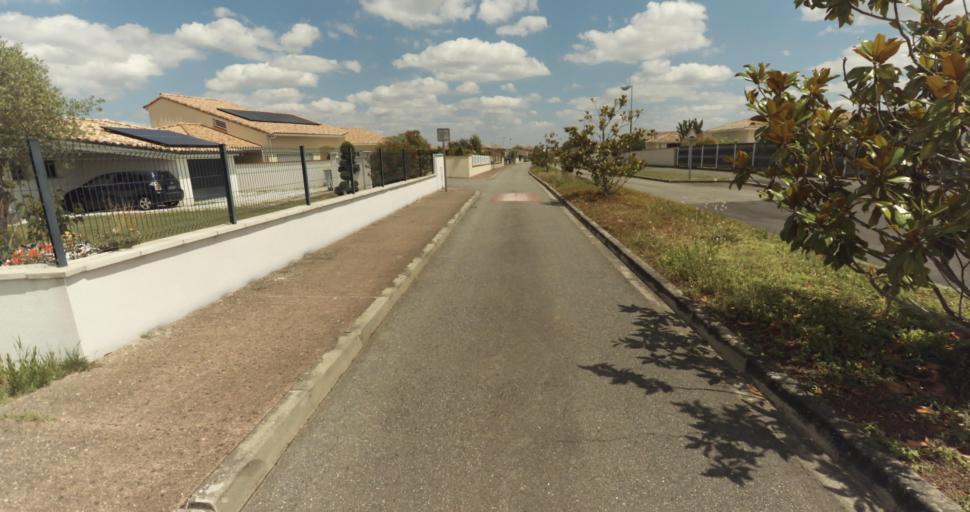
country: FR
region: Midi-Pyrenees
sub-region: Departement de la Haute-Garonne
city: Fontenilles
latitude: 43.5573
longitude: 1.1686
